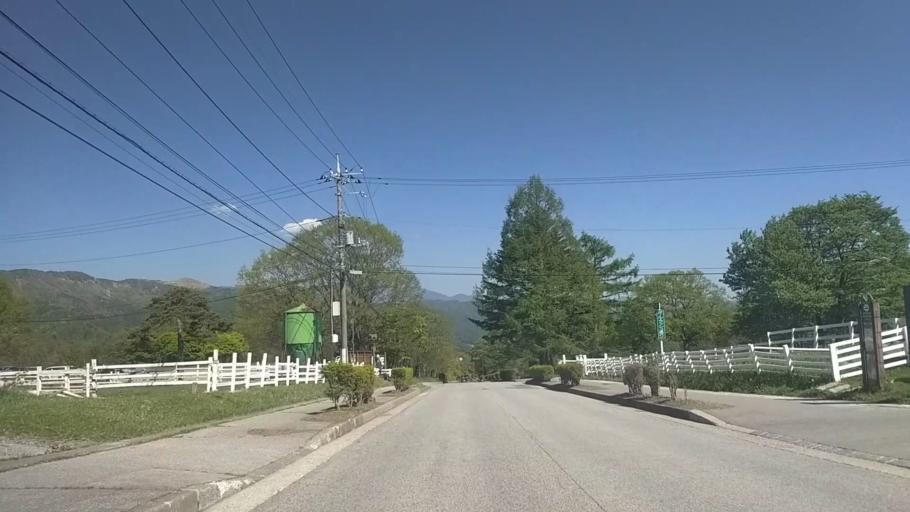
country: JP
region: Yamanashi
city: Nirasaki
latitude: 35.9226
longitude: 138.4271
